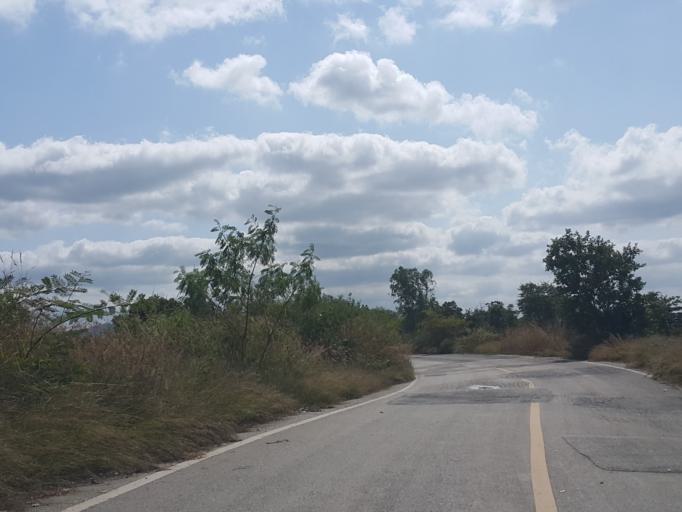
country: TH
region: Lamphun
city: Lamphun
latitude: 18.5514
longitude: 99.0866
